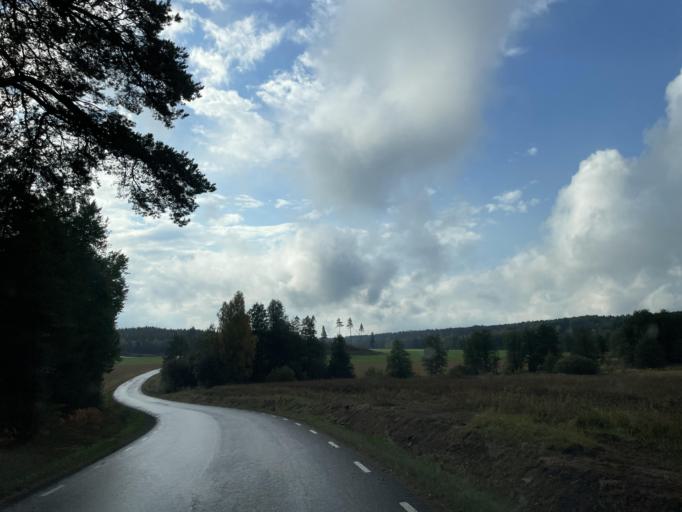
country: SE
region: Vaermland
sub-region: Karlstads Kommun
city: Skattkarr
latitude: 59.4291
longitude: 13.6047
